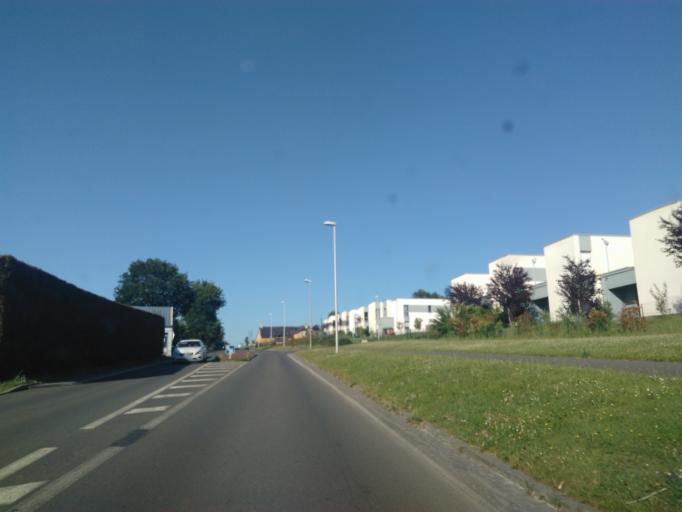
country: FR
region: Brittany
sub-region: Departement d'Ille-et-Vilaine
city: Geveze
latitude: 48.2233
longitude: -1.7823
